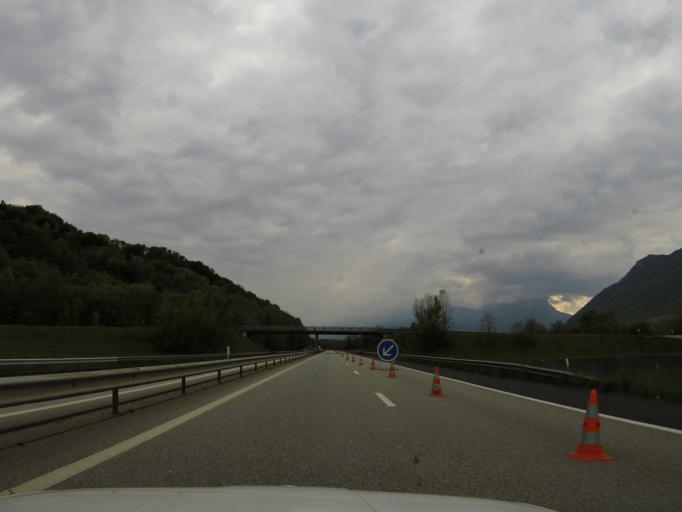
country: FR
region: Rhone-Alpes
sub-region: Departement de la Savoie
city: Coise-Saint-Jean-Pied-Gauthier
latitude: 45.5292
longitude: 6.1210
